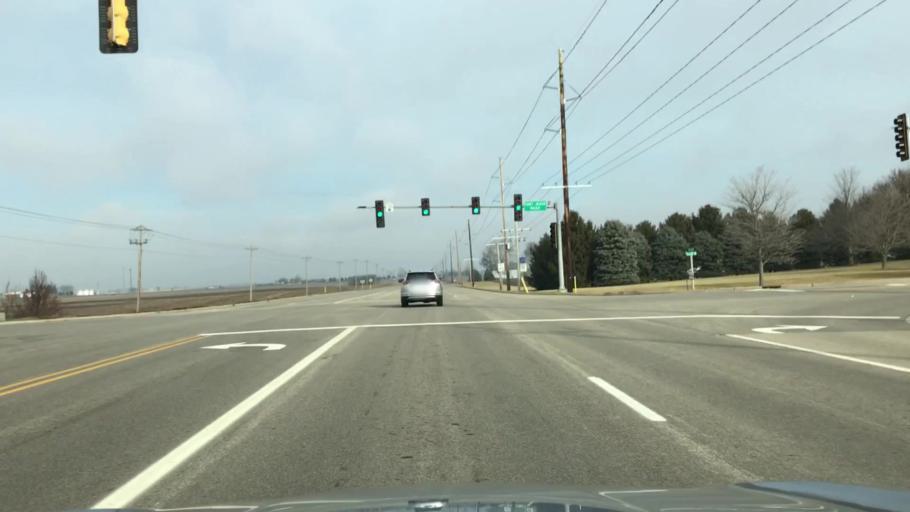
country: US
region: Illinois
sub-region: McLean County
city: Normal
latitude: 40.5171
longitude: -88.9029
